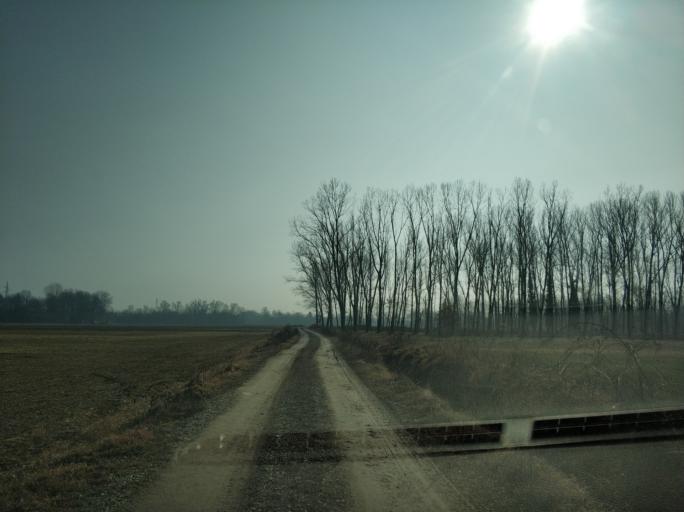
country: IT
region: Piedmont
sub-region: Provincia di Torino
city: Rivarossa
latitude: 45.2501
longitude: 7.7322
